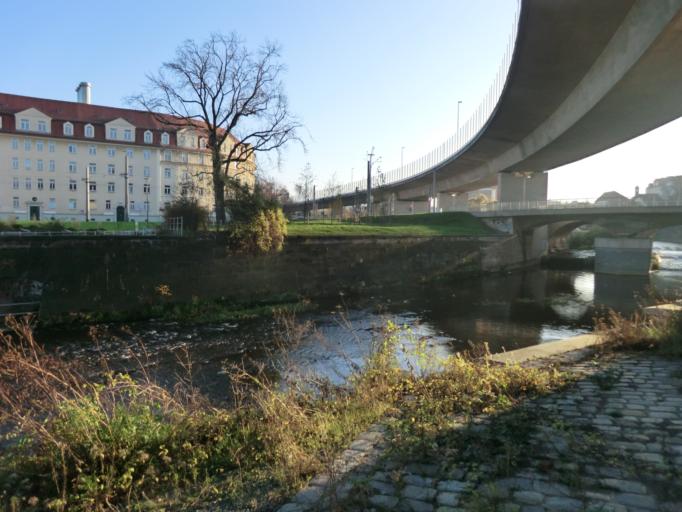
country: DE
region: Saxony
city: Dresden
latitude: 51.0441
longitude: 13.7054
